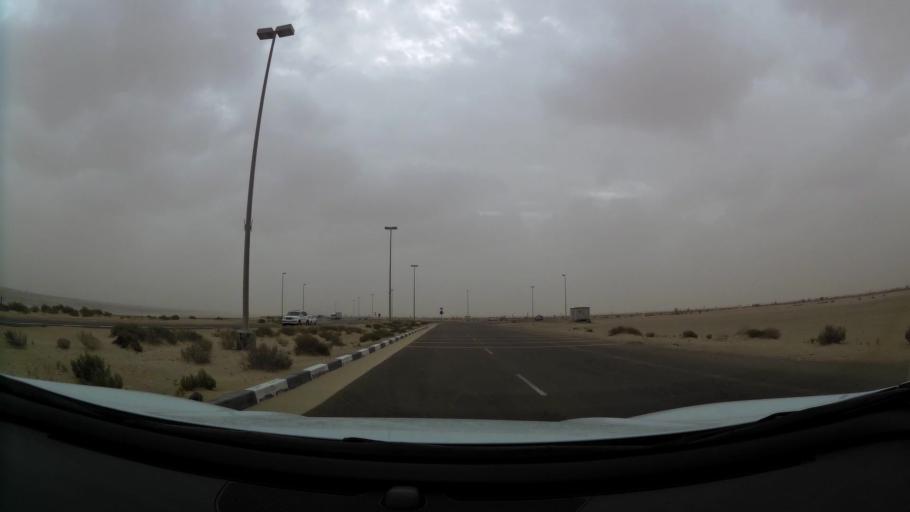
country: AE
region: Abu Dhabi
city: Abu Dhabi
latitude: 24.4618
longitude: 54.6882
